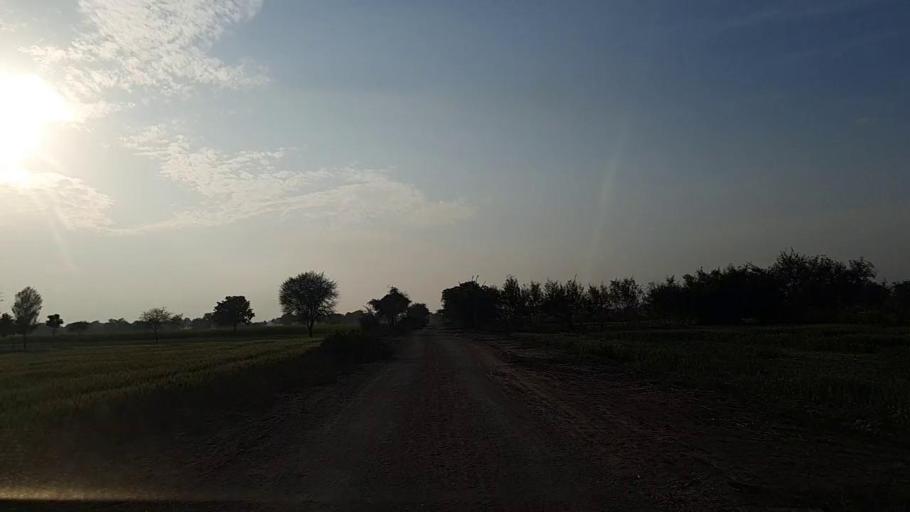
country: PK
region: Sindh
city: Jam Sahib
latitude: 26.3954
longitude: 68.5324
